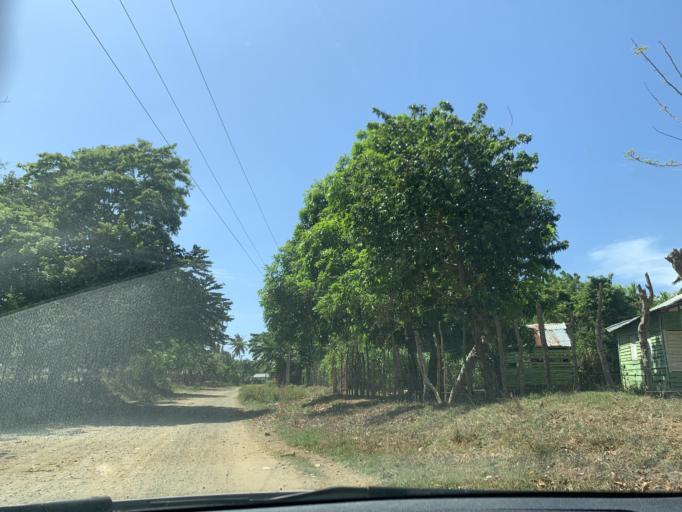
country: DO
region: Puerto Plata
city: Luperon
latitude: 19.8872
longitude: -70.8750
